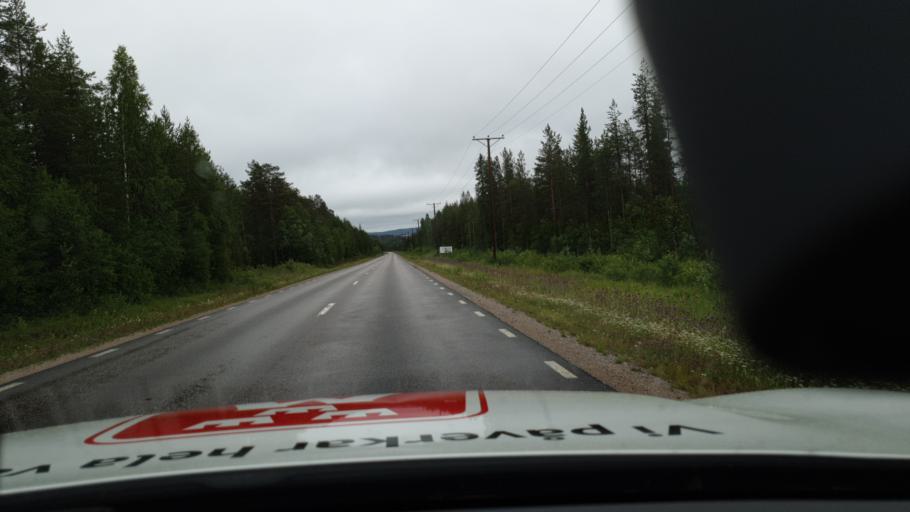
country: SE
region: Norrbotten
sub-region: Overtornea Kommun
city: OEvertornea
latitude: 66.3979
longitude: 23.5786
